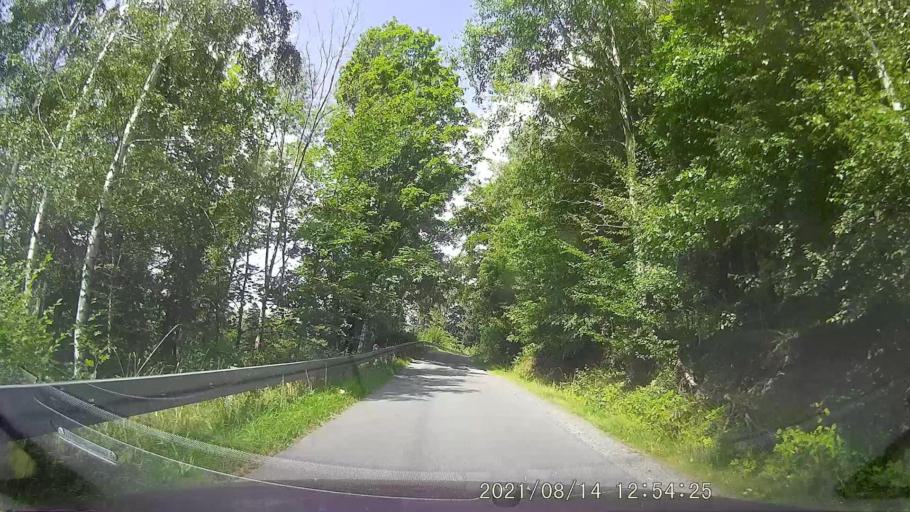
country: PL
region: Lower Silesian Voivodeship
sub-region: Powiat klodzki
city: Ladek-Zdroj
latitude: 50.3266
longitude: 16.8252
